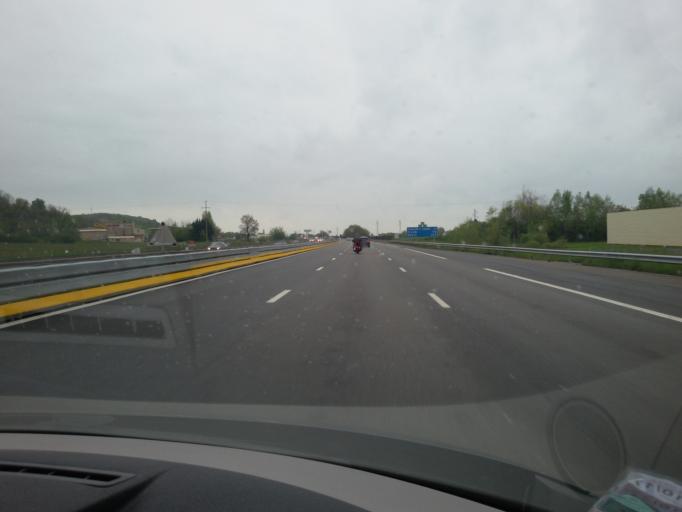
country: FR
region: Bourgogne
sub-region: Departement de Saone-et-Loire
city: Saint-Martin-Belle-Roche
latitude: 46.3768
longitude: 4.8444
